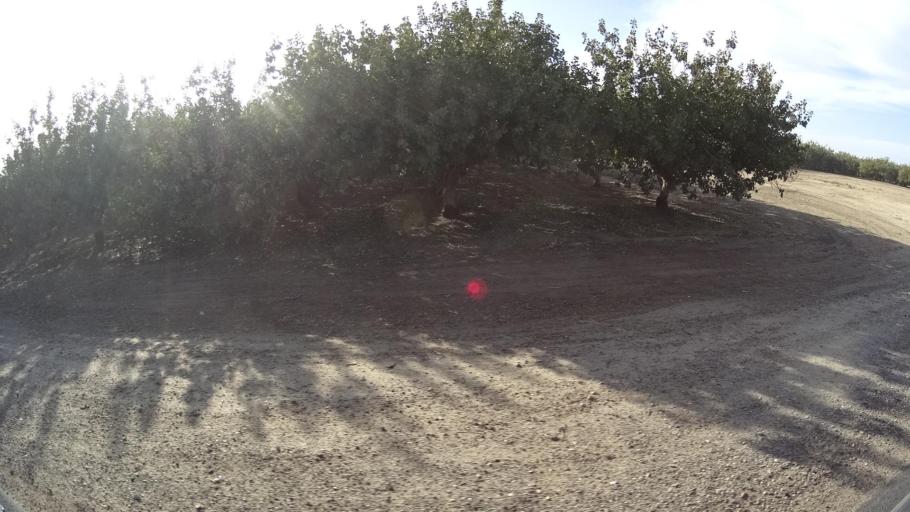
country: US
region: California
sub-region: Kern County
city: McFarland
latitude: 35.6021
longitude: -119.1663
